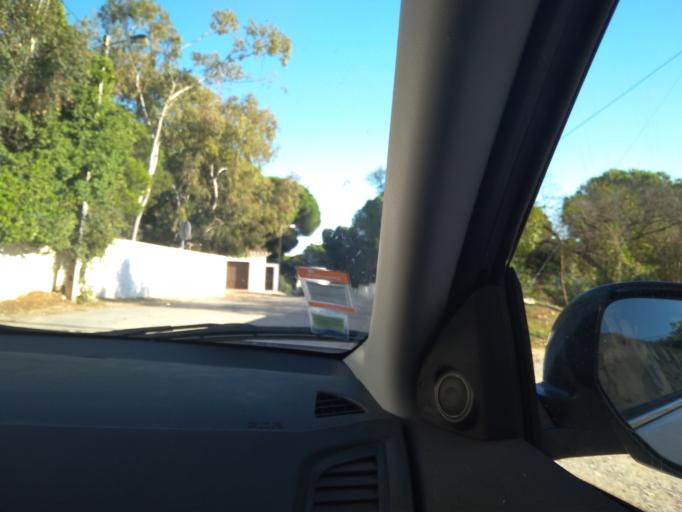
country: PT
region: Faro
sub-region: Albufeira
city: Albufeira
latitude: 37.0899
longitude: -8.2158
